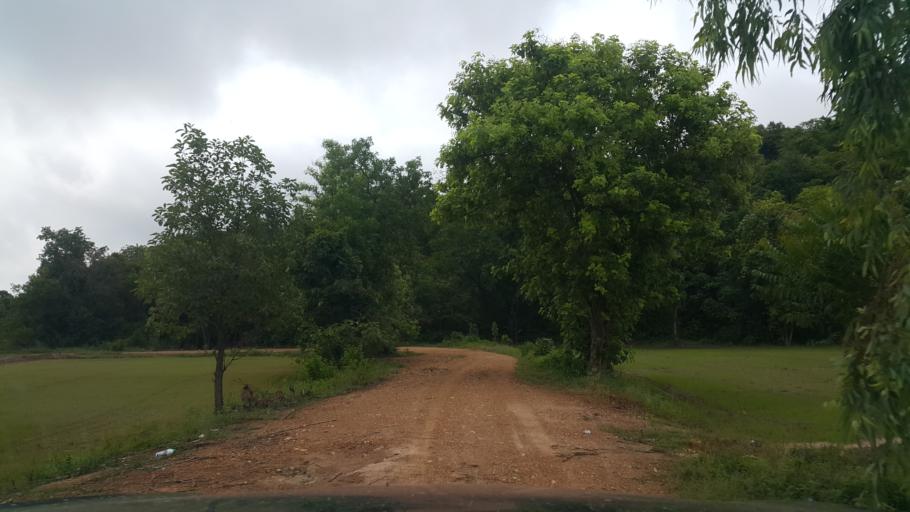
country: TH
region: Sukhothai
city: Sawankhalok
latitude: 17.3057
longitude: 99.7124
